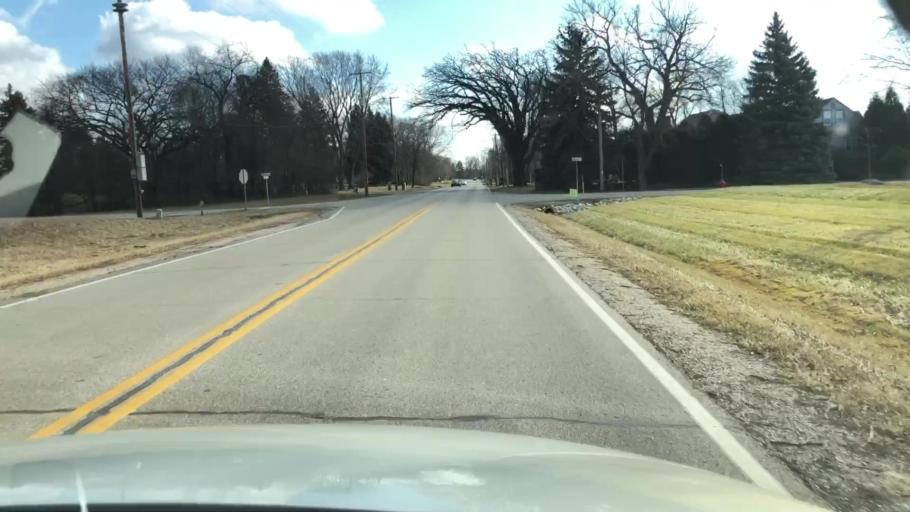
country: US
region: Wisconsin
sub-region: Waukesha County
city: Waukesha
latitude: 43.0434
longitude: -88.1774
